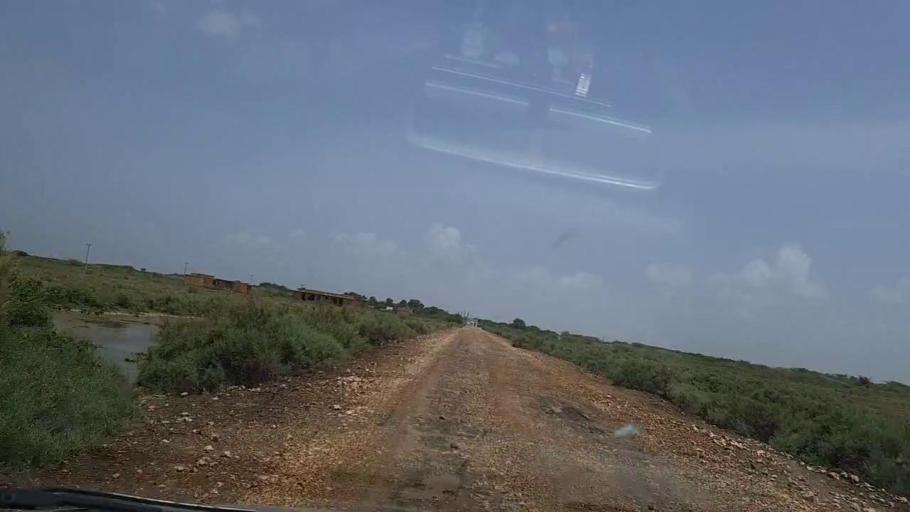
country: PK
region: Sindh
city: Keti Bandar
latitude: 24.1524
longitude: 67.5316
